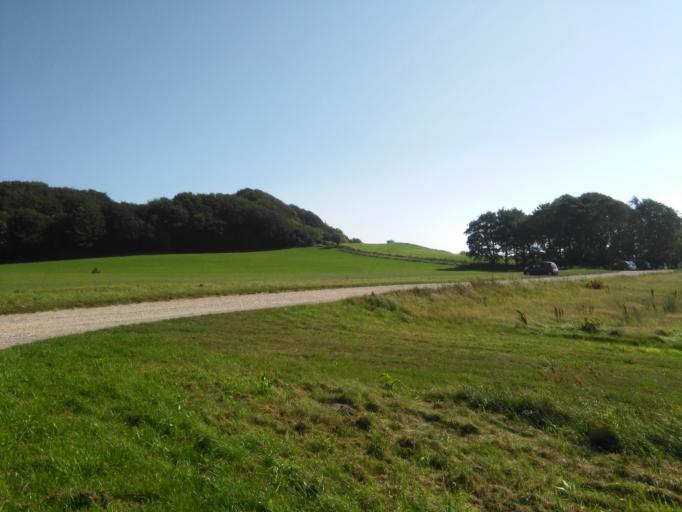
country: DK
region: Central Jutland
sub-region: Syddjurs Kommune
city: Ebeltoft
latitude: 56.2452
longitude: 10.7792
